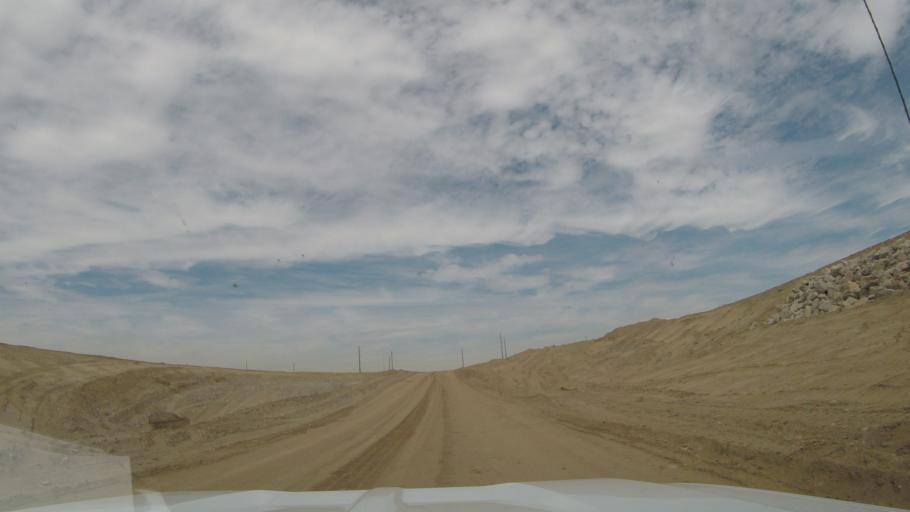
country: US
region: Arizona
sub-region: Maricopa County
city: Laveen
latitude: 33.4033
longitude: -112.1928
